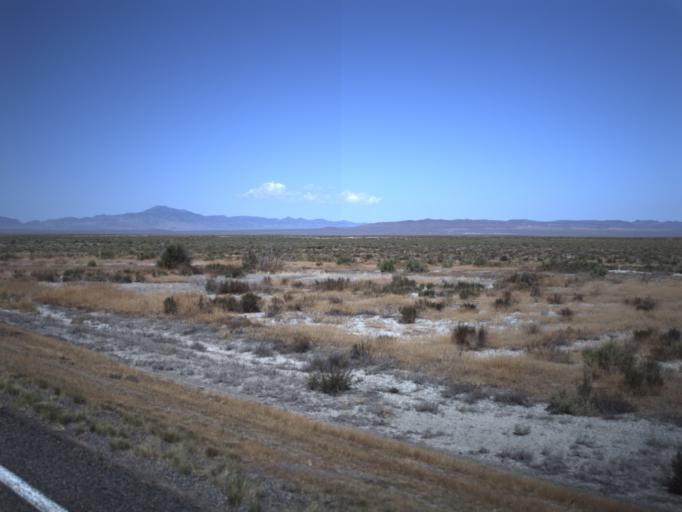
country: US
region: Utah
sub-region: Millard County
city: Delta
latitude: 39.3062
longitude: -112.7963
